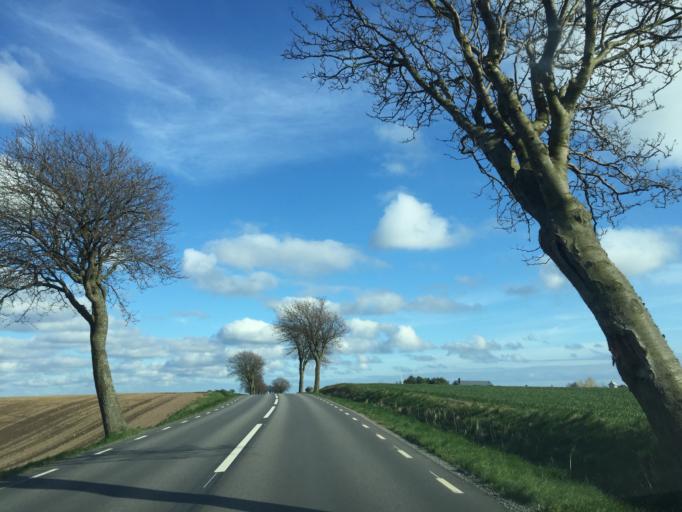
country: SE
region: Skane
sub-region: Skurups Kommun
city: Skivarp
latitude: 55.4214
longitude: 13.6252
